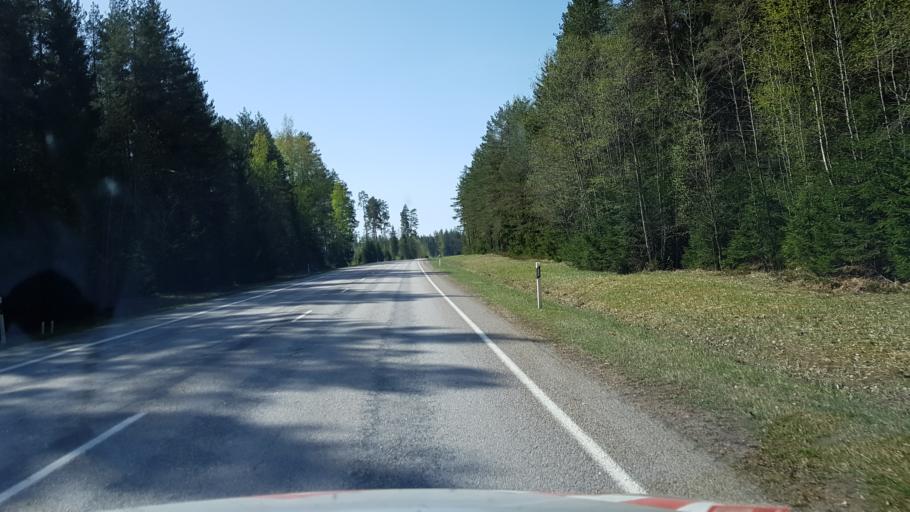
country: EE
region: Valgamaa
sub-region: Valga linn
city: Valga
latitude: 57.8296
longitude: 26.0571
